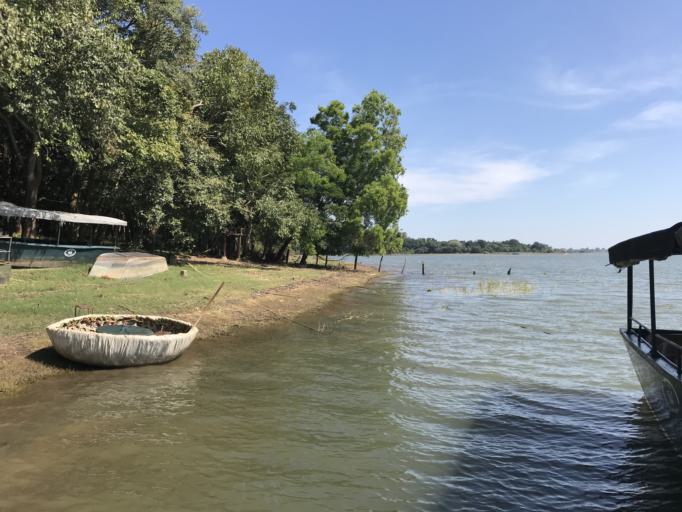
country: IN
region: Karnataka
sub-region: Mysore
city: Sargur
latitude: 11.9368
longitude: 76.2707
